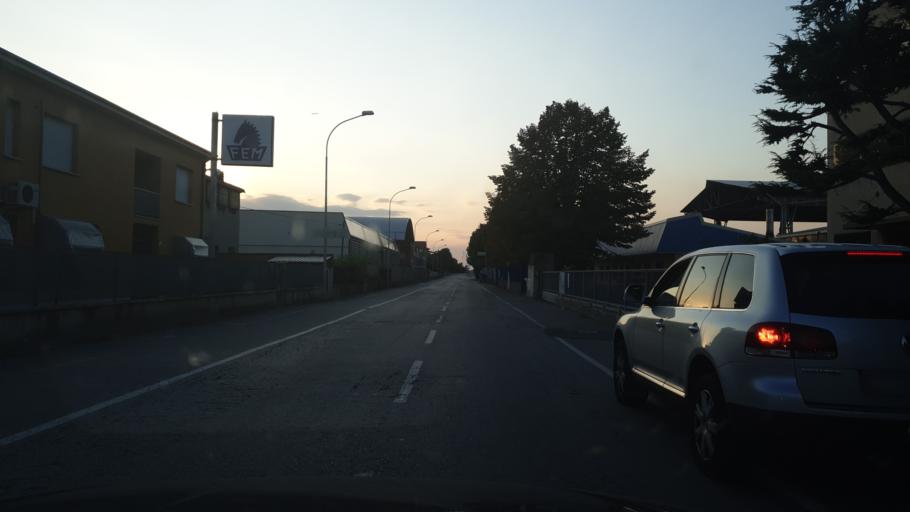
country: IT
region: Emilia-Romagna
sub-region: Provincia di Bologna
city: Quarto Inferiore
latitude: 44.5494
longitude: 11.3921
